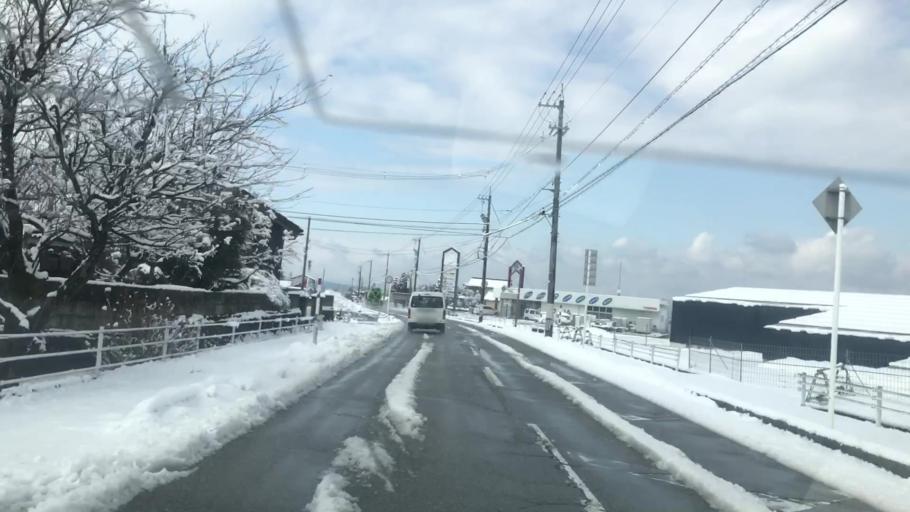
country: JP
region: Toyama
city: Toyama-shi
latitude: 36.6262
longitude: 137.2427
